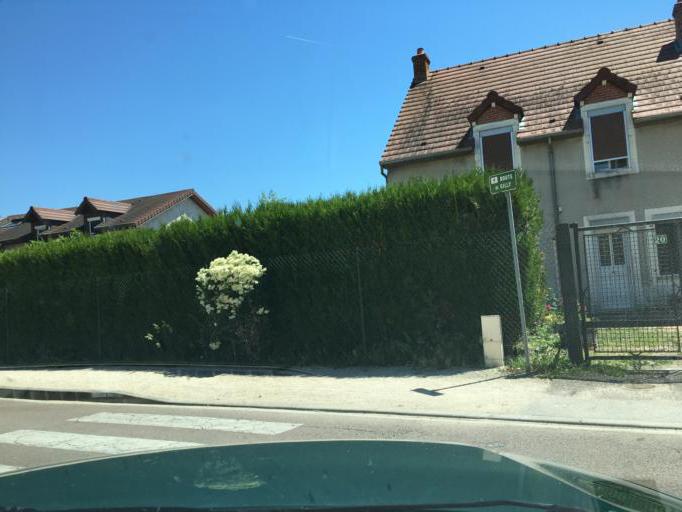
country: FR
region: Bourgogne
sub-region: Departement de la Cote-d'Or
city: Nuits-Saint-Georges
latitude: 47.1676
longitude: 4.9818
